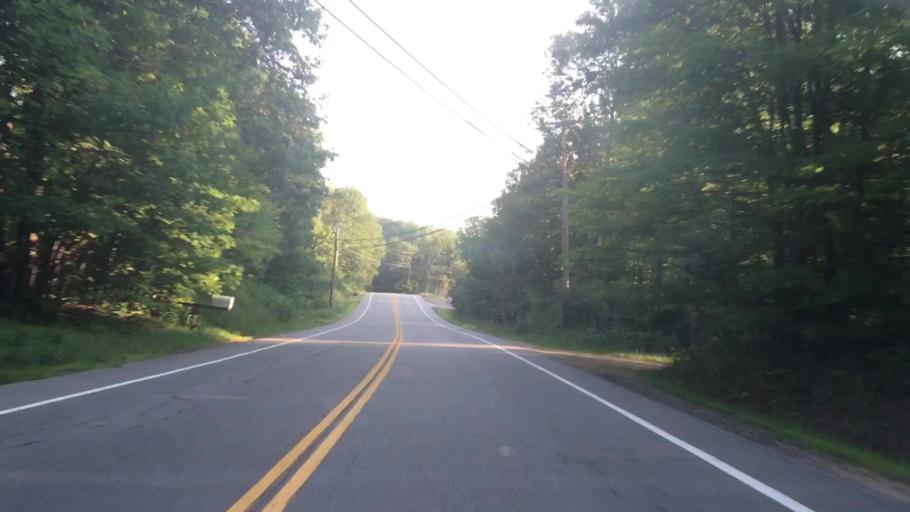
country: US
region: New Hampshire
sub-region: Belknap County
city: Gilmanton
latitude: 43.4637
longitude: -71.4214
